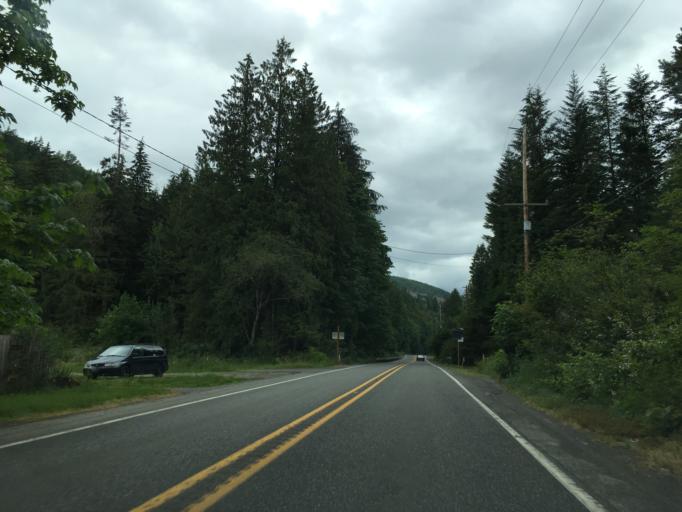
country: US
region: Washington
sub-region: Whatcom County
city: Peaceful Valley
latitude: 48.8683
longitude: -122.1532
